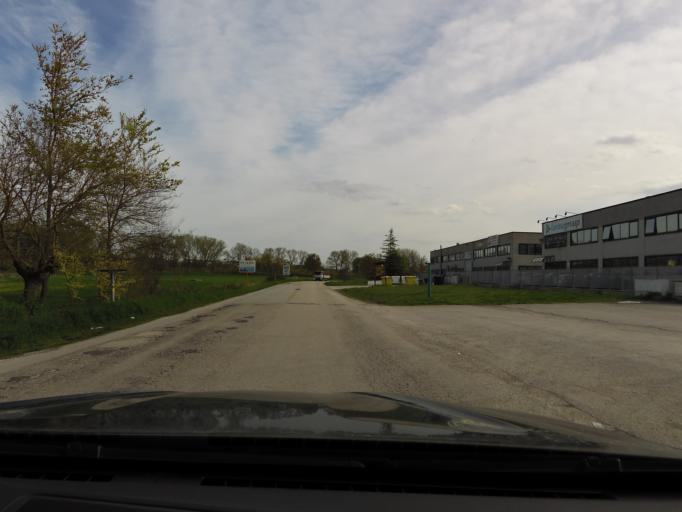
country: IT
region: The Marches
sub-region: Provincia di Ancona
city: Camerano
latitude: 43.5239
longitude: 13.5256
